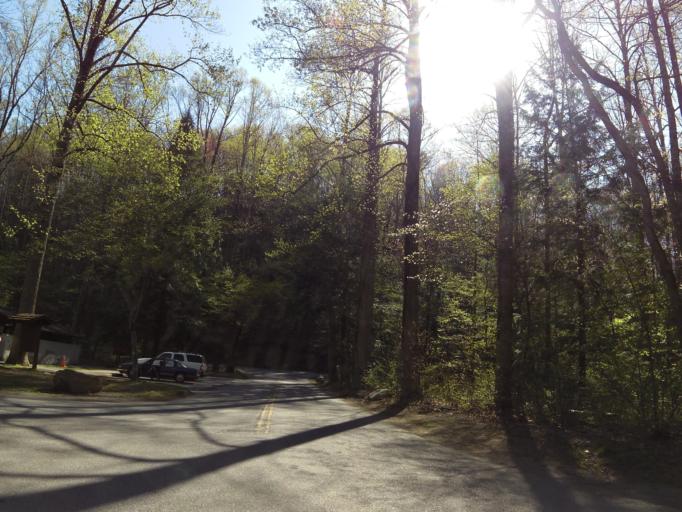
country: US
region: Tennessee
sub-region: Sevier County
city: Gatlinburg
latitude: 35.6787
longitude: -83.6479
